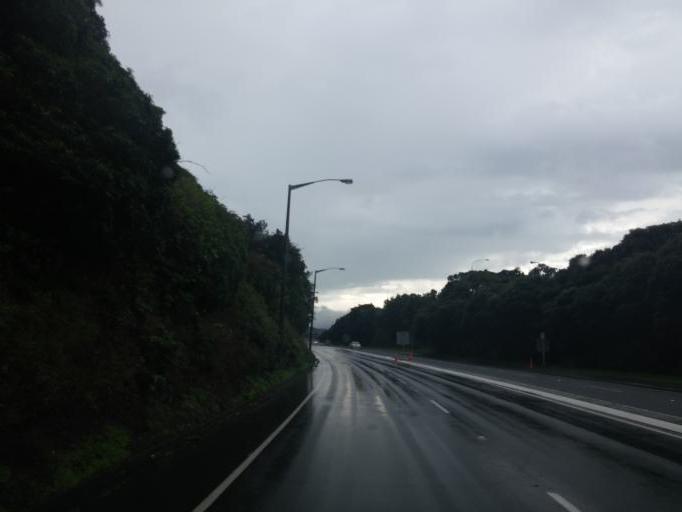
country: NZ
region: Wellington
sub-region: Wellington City
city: Wellington
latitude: -41.2523
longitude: 174.8052
